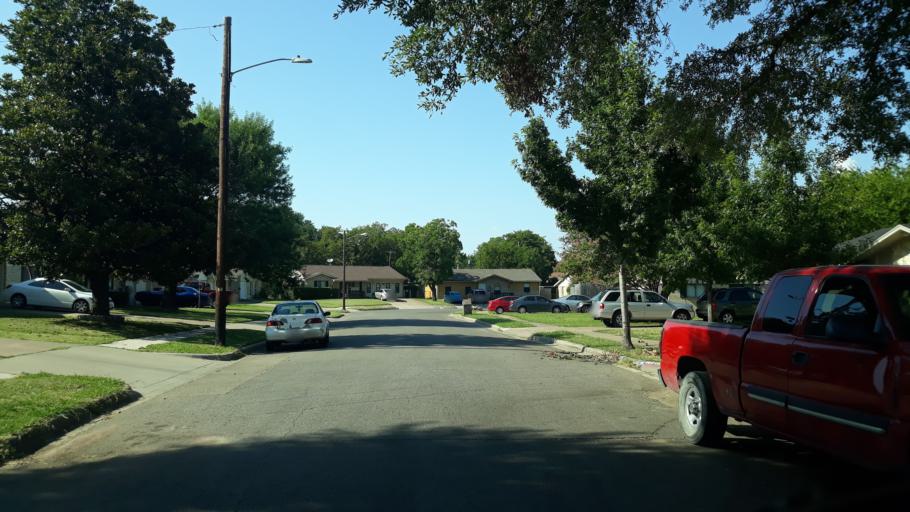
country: US
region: Texas
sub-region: Dallas County
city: Irving
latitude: 32.8490
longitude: -97.0065
